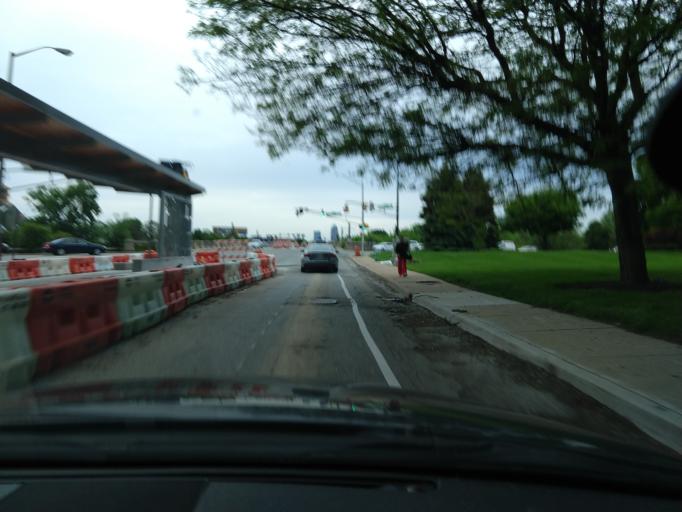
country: US
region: Indiana
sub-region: Marion County
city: Indianapolis
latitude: 39.8045
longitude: -86.1567
